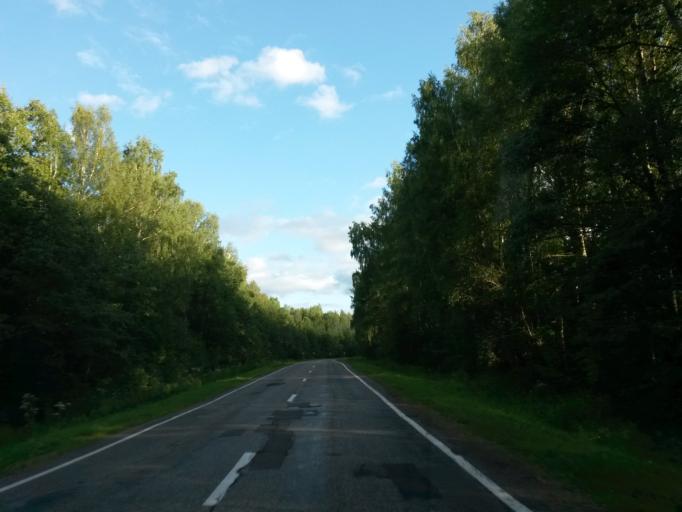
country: RU
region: Jaroslavl
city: Tutayev
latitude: 57.9192
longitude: 39.5143
